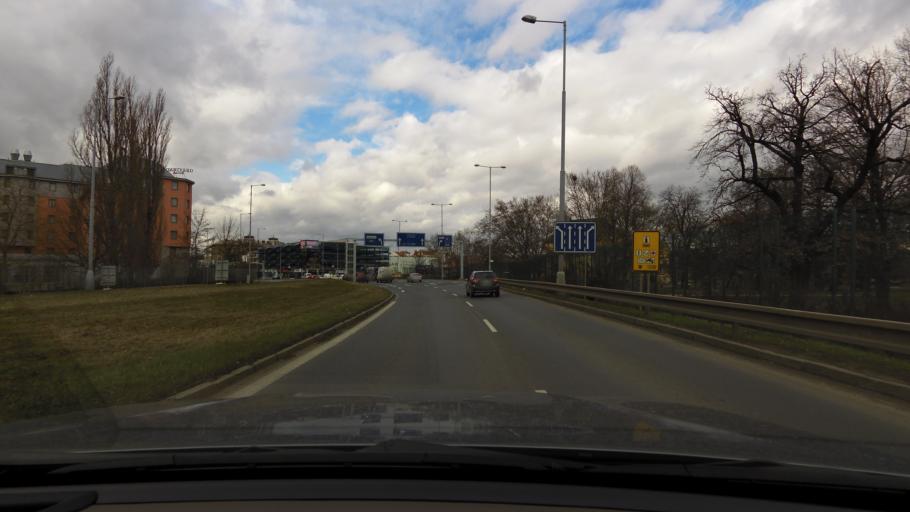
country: CZ
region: Plzensky
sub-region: Okres Plzen-Mesto
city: Pilsen
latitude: 49.7486
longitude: 13.3836
